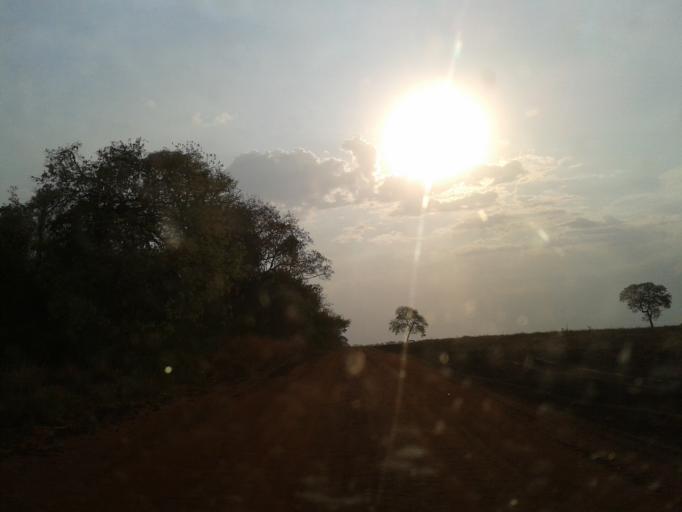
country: BR
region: Minas Gerais
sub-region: Capinopolis
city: Capinopolis
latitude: -18.7565
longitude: -49.6947
